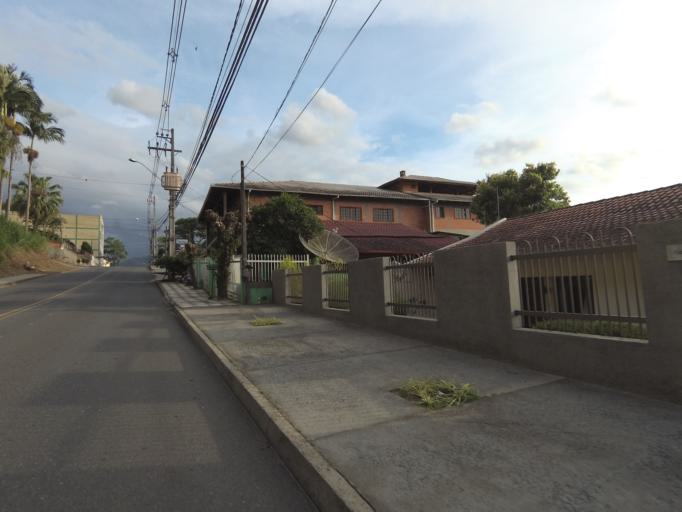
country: BR
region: Santa Catarina
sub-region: Blumenau
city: Blumenau
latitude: -26.9005
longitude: -49.1265
